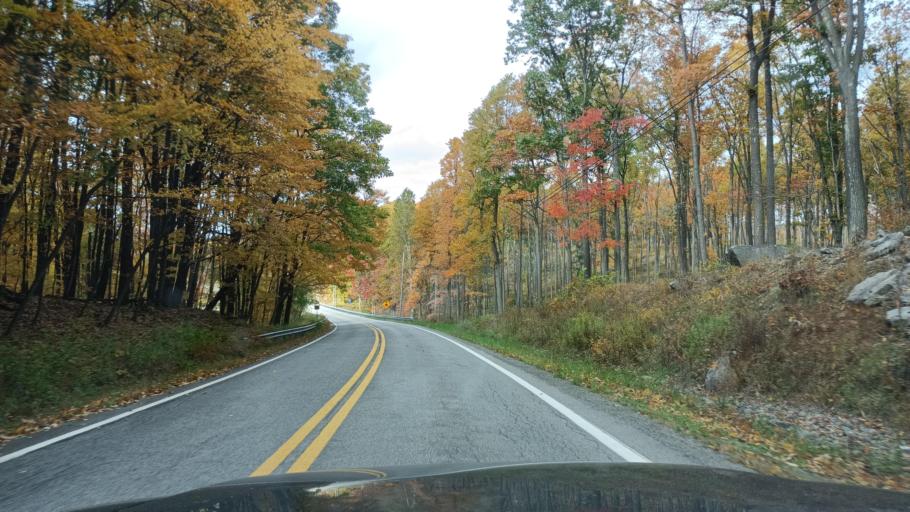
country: US
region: West Virginia
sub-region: Monongalia County
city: Cheat Lake
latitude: 39.6599
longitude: -79.7736
